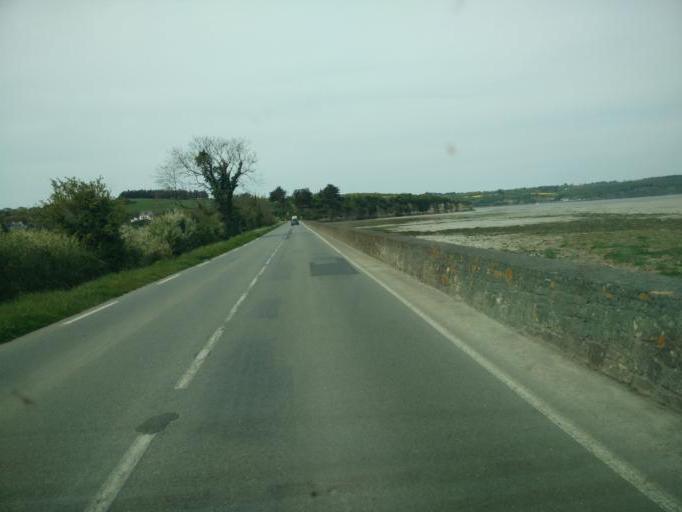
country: FR
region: Brittany
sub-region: Departement des Cotes-d'Armor
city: Matignon
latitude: 48.6108
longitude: -2.3171
